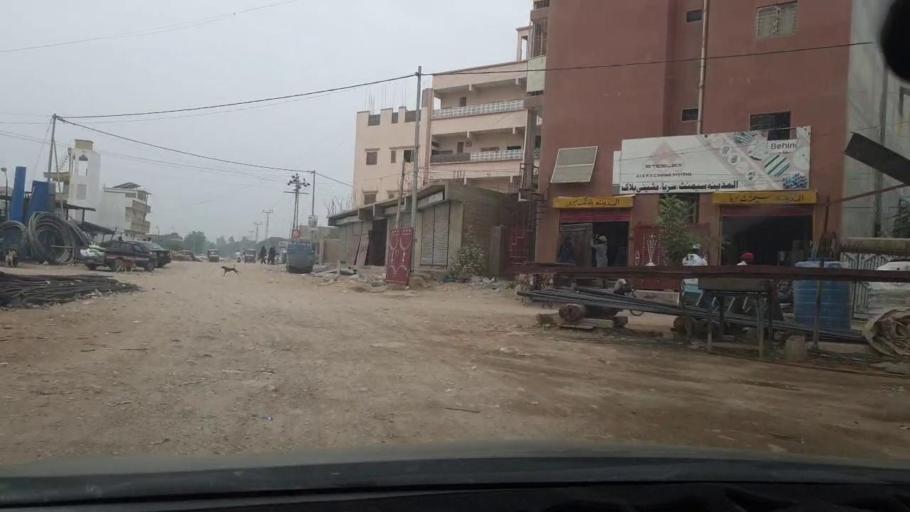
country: PK
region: Sindh
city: Malir Cantonment
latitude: 24.9218
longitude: 67.2597
